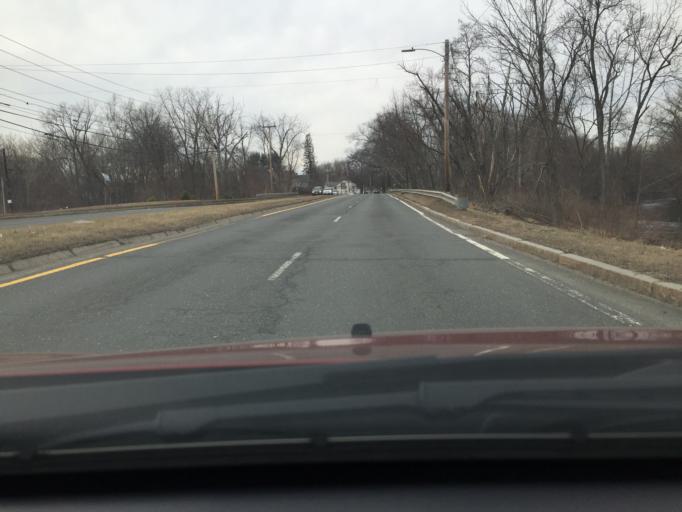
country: US
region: Massachusetts
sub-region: Hampden County
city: Westfield
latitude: 42.1158
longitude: -72.7324
